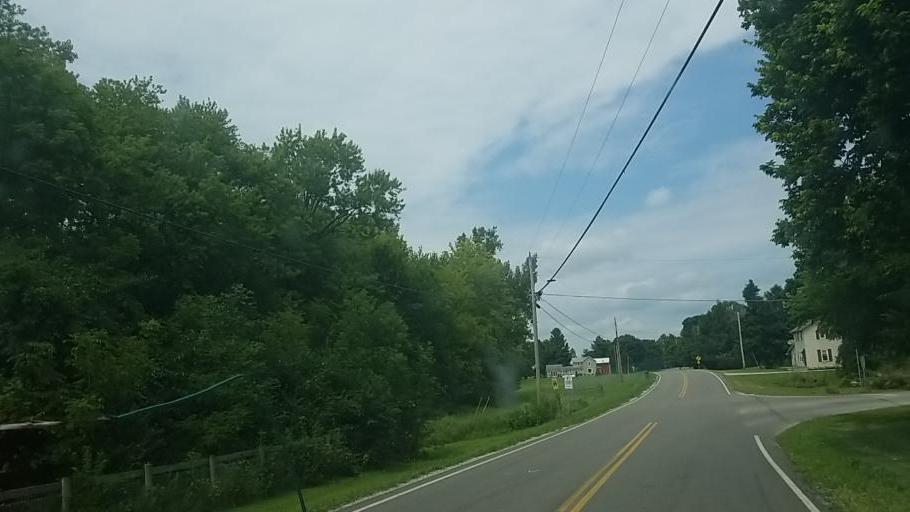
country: US
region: Ohio
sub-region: Pickaway County
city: Ashville
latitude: 39.7466
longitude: -82.9155
